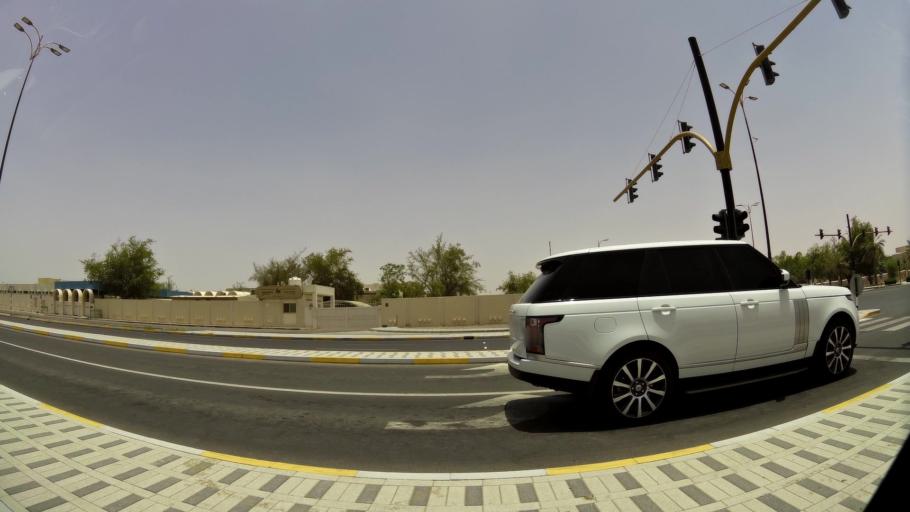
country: AE
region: Abu Dhabi
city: Al Ain
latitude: 24.2145
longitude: 55.7248
